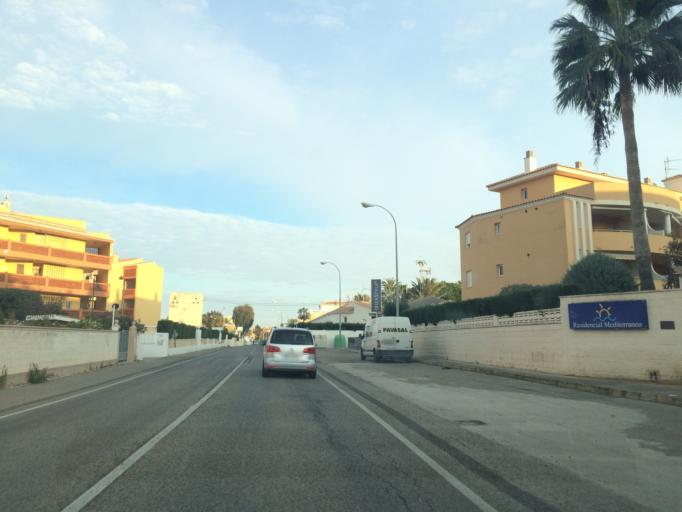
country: ES
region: Valencia
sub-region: Provincia de Alicante
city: Denia
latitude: 38.8565
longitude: 0.0682
